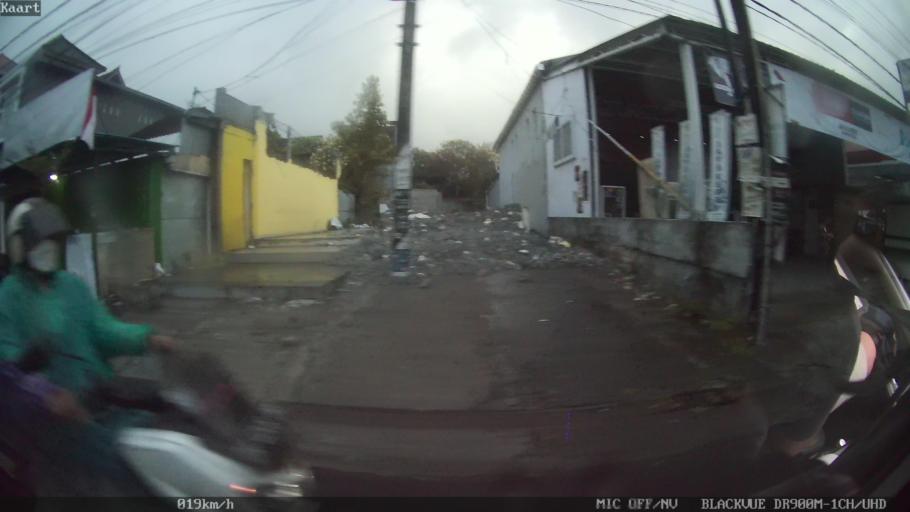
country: ID
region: Bali
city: Banjar Batur
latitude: -8.5892
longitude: 115.2156
